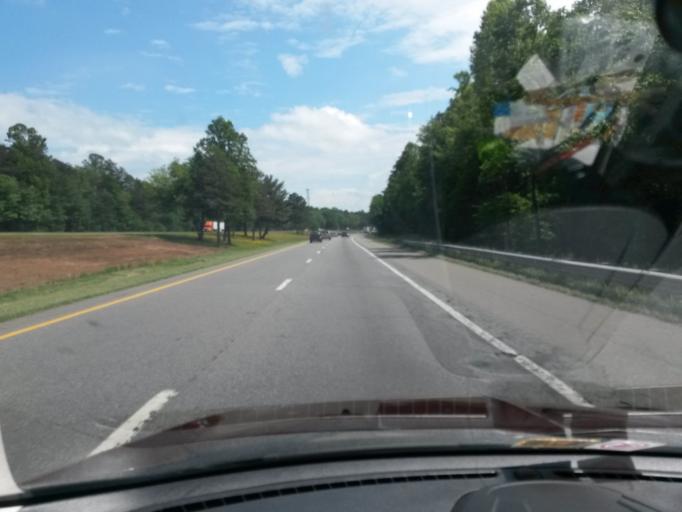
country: US
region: North Carolina
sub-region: Surry County
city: Dobson
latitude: 36.3499
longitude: -80.7967
